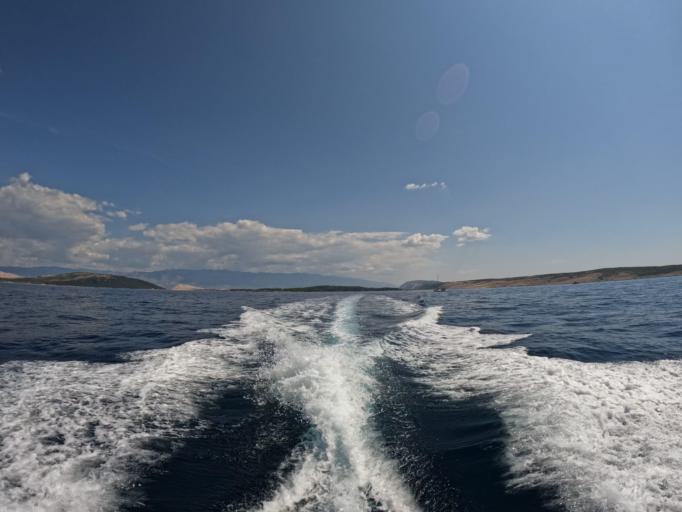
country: HR
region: Primorsko-Goranska
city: Lopar
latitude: 44.8606
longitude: 14.6949
